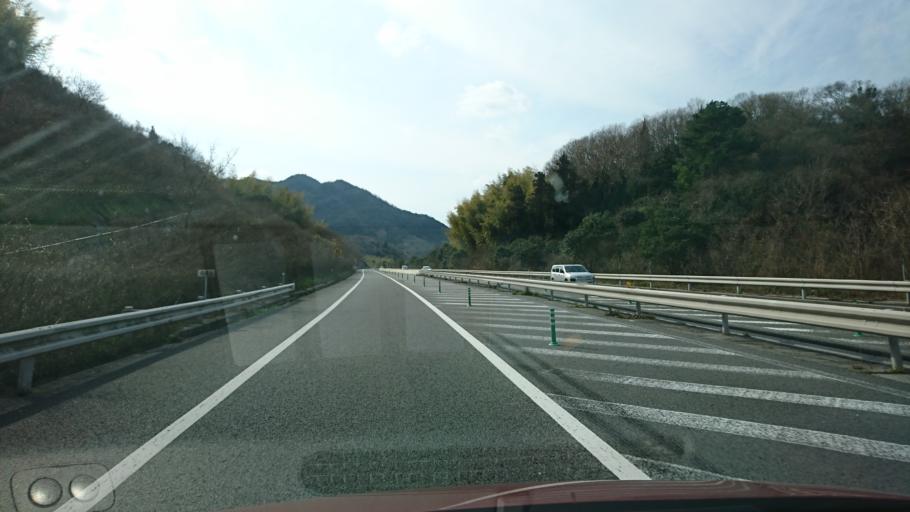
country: JP
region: Hiroshima
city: Innoshima
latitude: 34.1388
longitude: 133.0546
